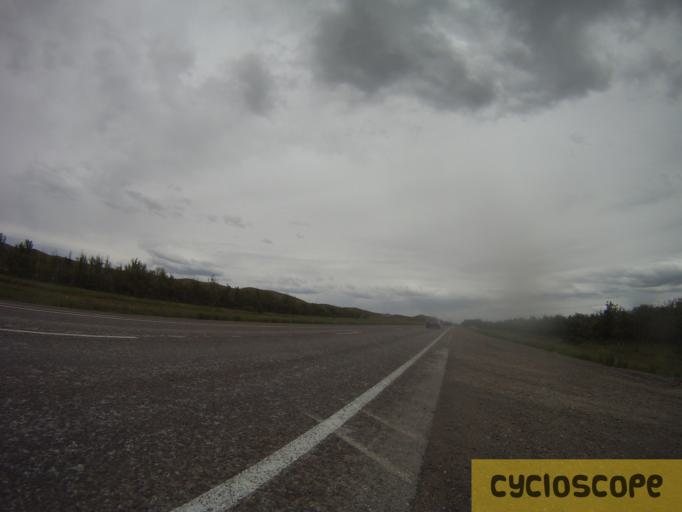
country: KZ
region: Zhambyl
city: Georgiyevka
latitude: 43.2959
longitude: 74.8801
